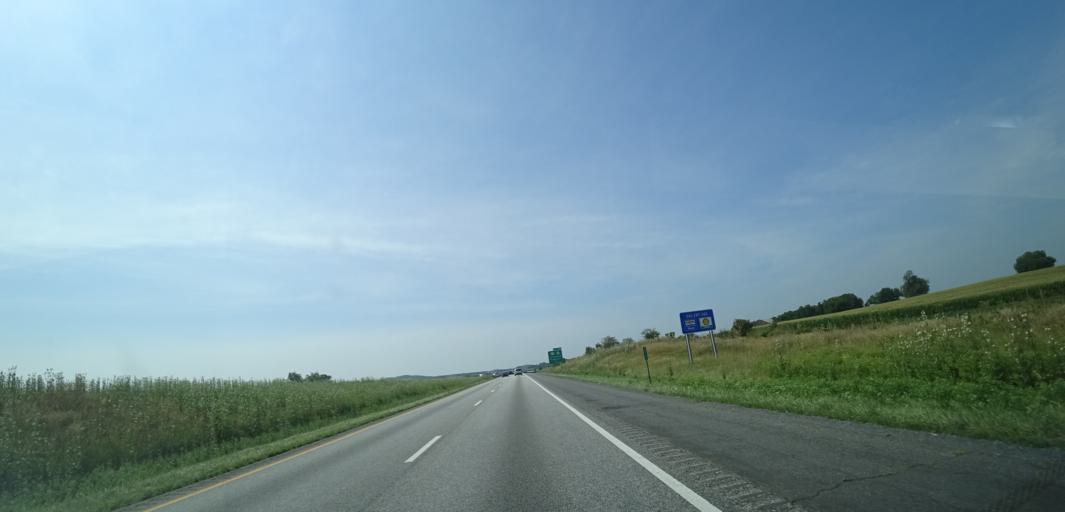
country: US
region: Virginia
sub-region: Rockingham County
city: Dayton
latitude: 38.3760
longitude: -78.9189
